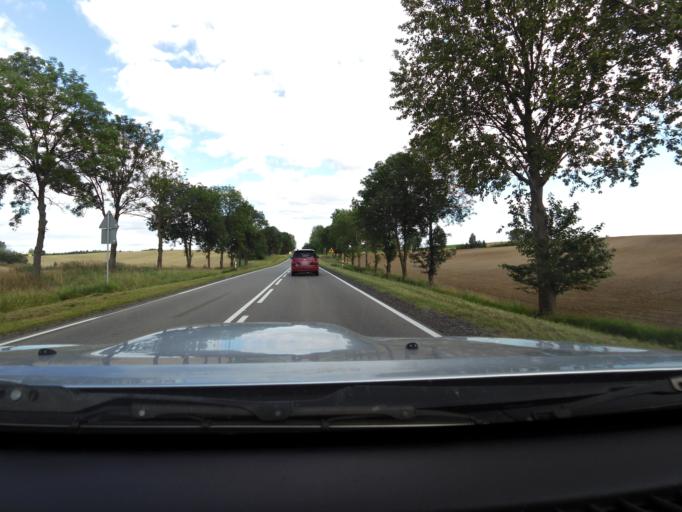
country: PL
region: Podlasie
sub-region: Powiat grajewski
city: Rajgrod
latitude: 53.8619
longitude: 22.7027
